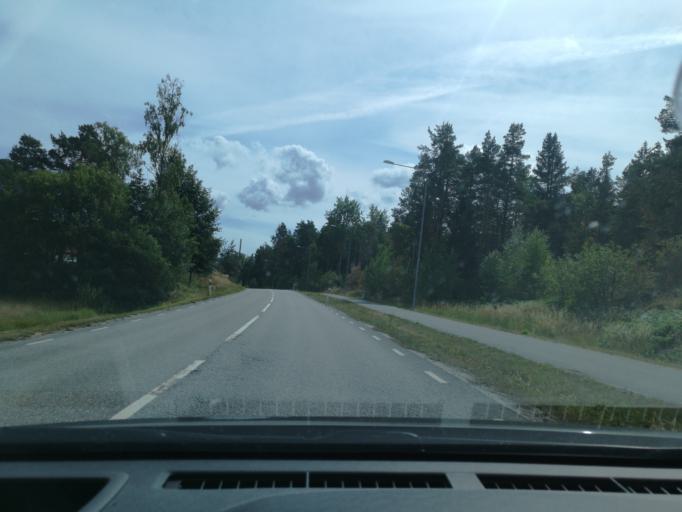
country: SE
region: Stockholm
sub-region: Sigtuna Kommun
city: Rosersberg
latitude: 59.5991
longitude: 17.8823
